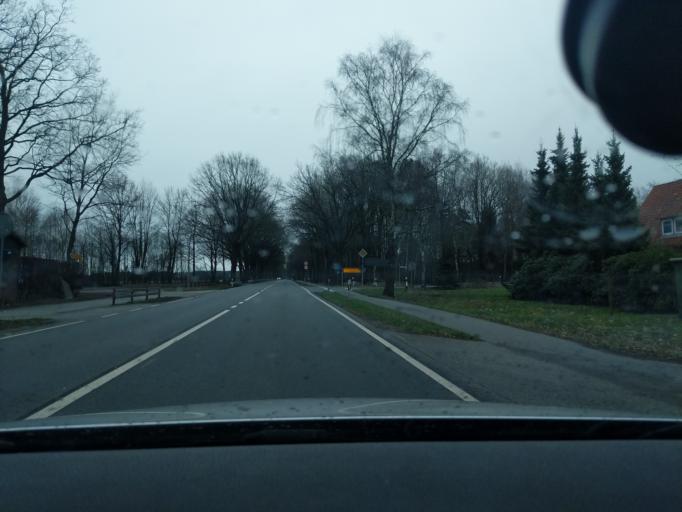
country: DE
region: Lower Saxony
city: Dudenbuttel
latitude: 53.5507
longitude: 9.3499
